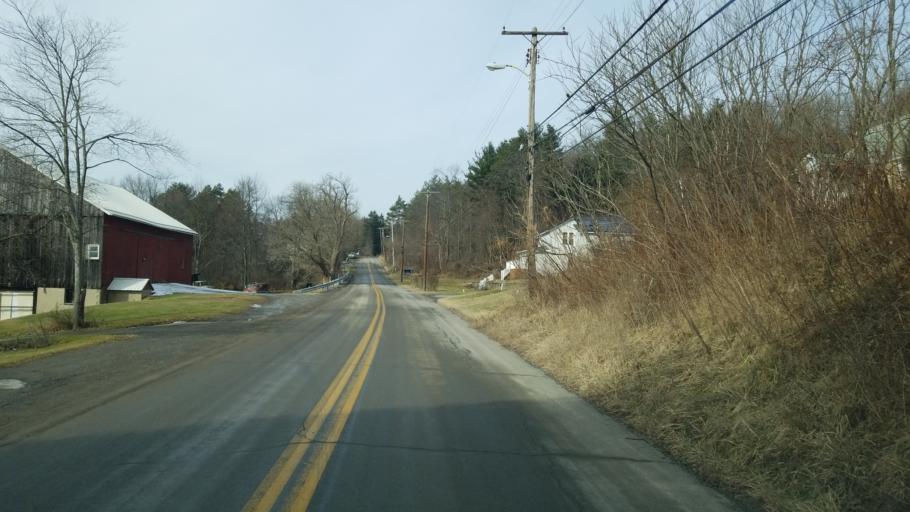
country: US
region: Pennsylvania
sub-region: Indiana County
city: Johnsonburg
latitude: 40.8235
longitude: -78.8306
